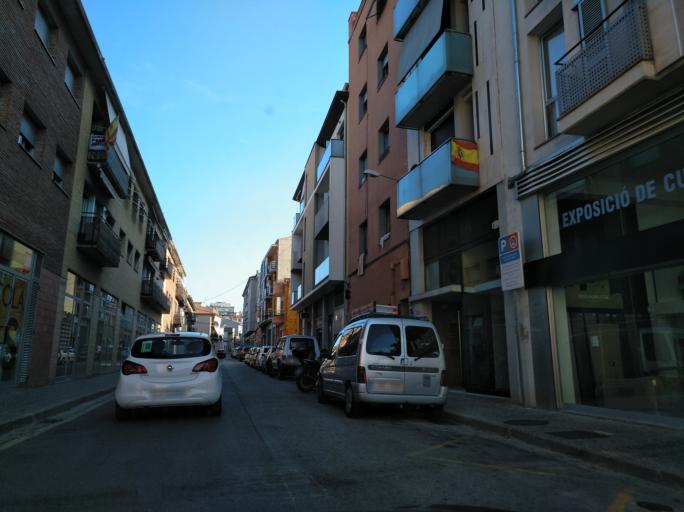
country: ES
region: Catalonia
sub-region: Provincia de Girona
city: Girona
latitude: 41.9709
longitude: 2.8215
